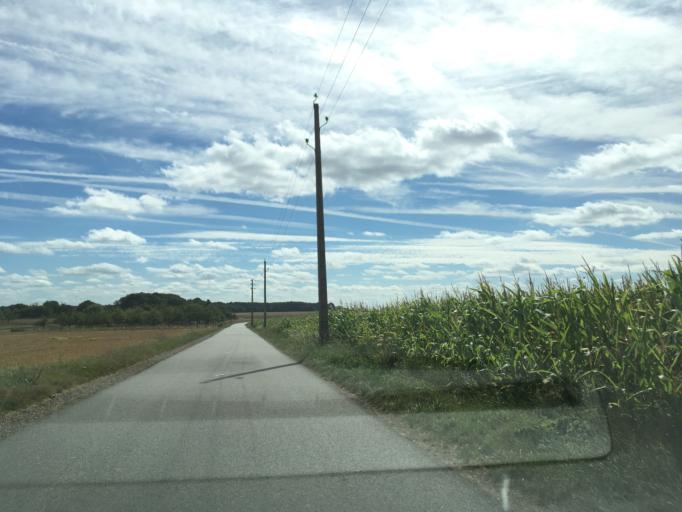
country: FR
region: Haute-Normandie
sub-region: Departement de l'Eure
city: Heudreville-sur-Eure
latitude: 49.1584
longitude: 1.2553
